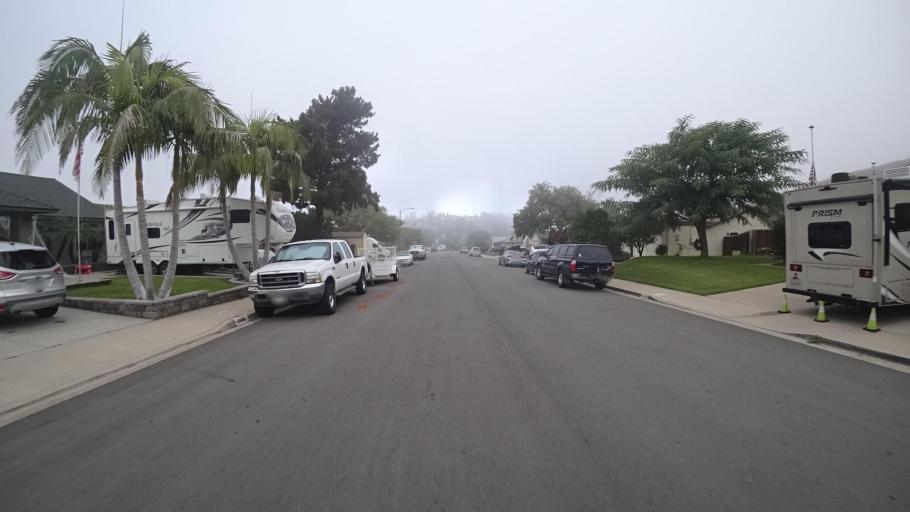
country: US
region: California
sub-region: San Diego County
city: Rancho San Diego
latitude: 32.7312
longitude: -116.9563
